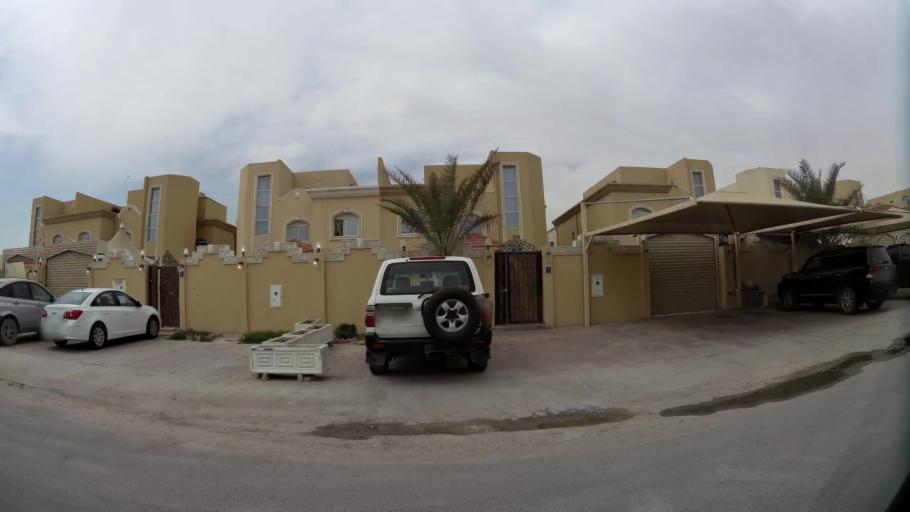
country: QA
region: Baladiyat ad Dawhah
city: Doha
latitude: 25.2202
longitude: 51.4739
